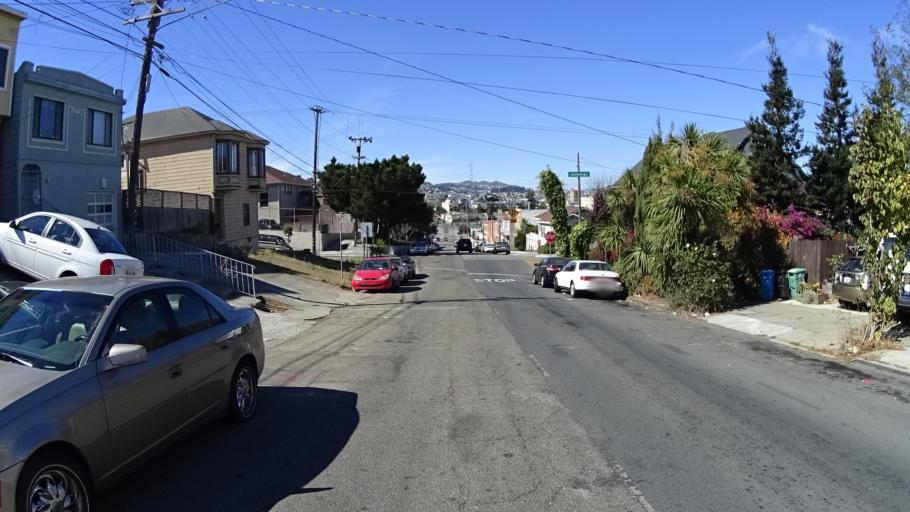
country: US
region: California
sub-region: San Mateo County
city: Brisbane
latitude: 37.7193
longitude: -122.3950
